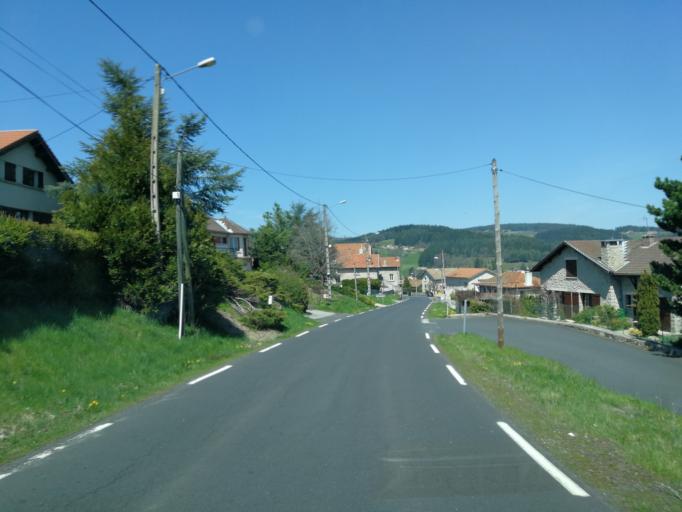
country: FR
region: Auvergne
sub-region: Departement de la Haute-Loire
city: Dunieres
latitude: 45.2108
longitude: 4.3460
